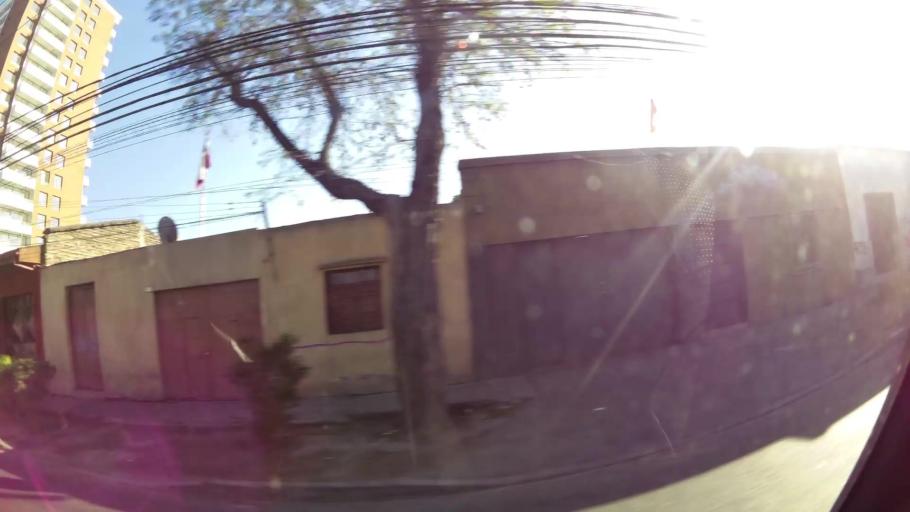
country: CL
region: Santiago Metropolitan
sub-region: Provincia de Santiago
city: Santiago
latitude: -33.4911
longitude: -70.6453
